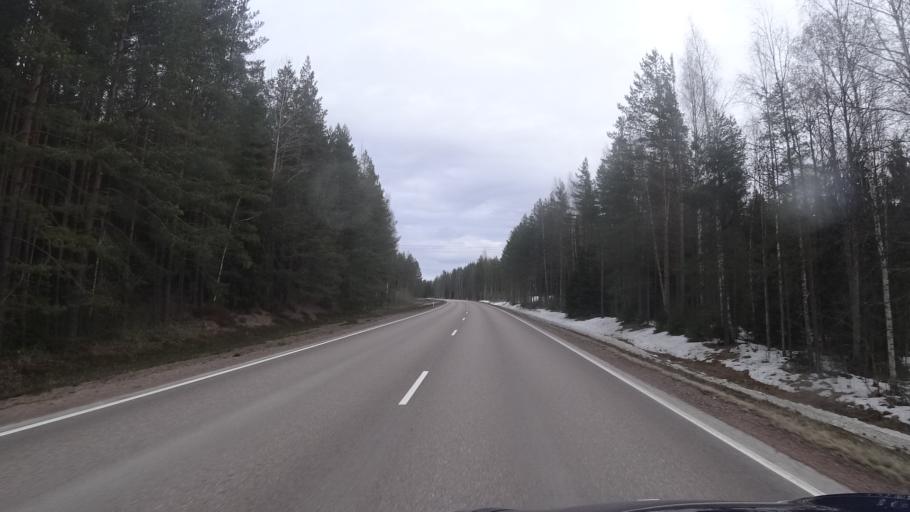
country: FI
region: Kymenlaakso
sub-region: Kouvola
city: Anjala
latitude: 60.6929
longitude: 26.6684
